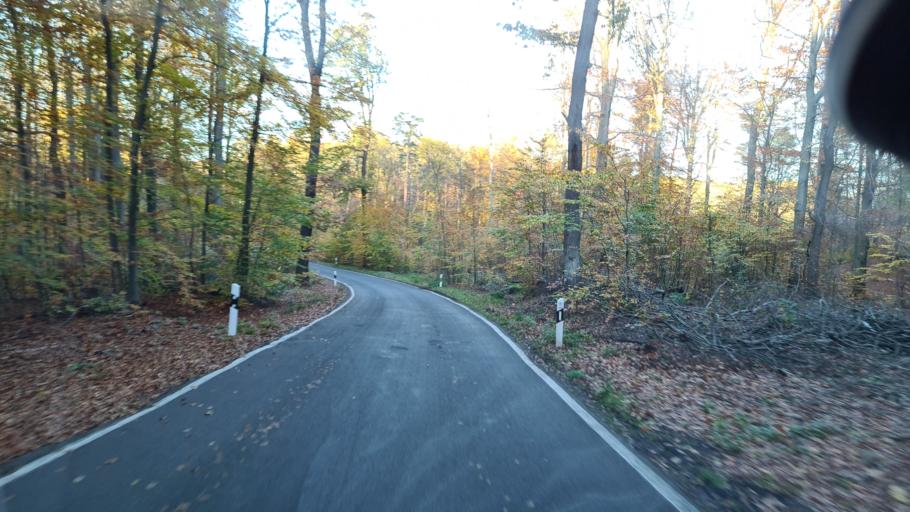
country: DE
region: Saxony
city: Dahlen
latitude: 51.4099
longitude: 13.0295
